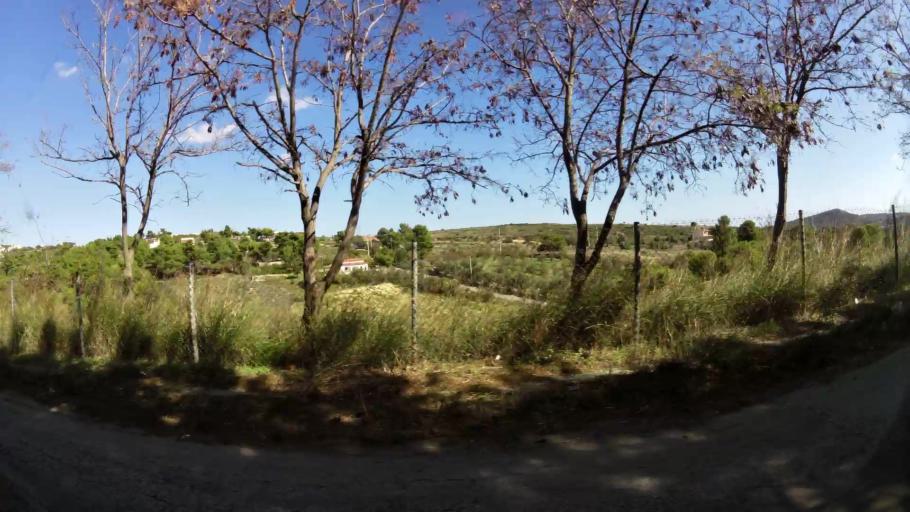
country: GR
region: Attica
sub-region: Nomarchia Anatolikis Attikis
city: Dioni
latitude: 38.0138
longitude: 23.9321
